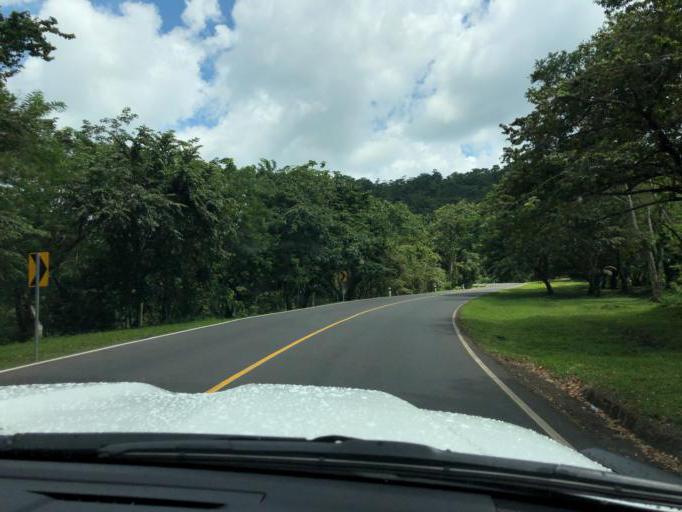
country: NI
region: Chontales
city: Villa Sandino
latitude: 11.9949
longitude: -84.9052
